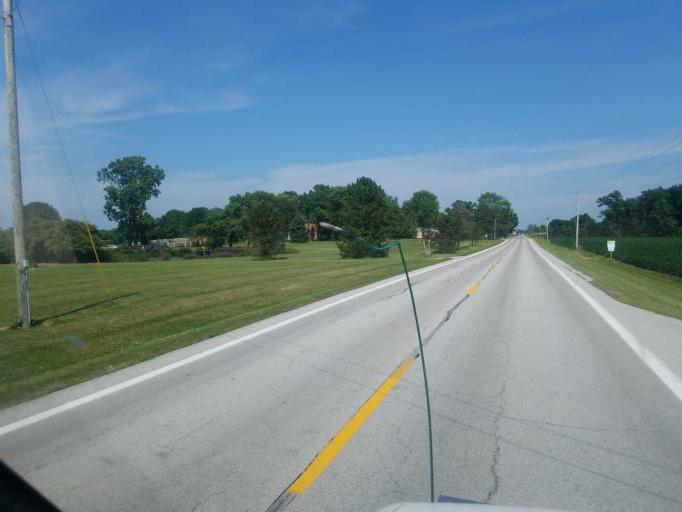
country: US
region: Ohio
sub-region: Shelby County
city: Botkins
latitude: 40.4965
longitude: -84.2531
